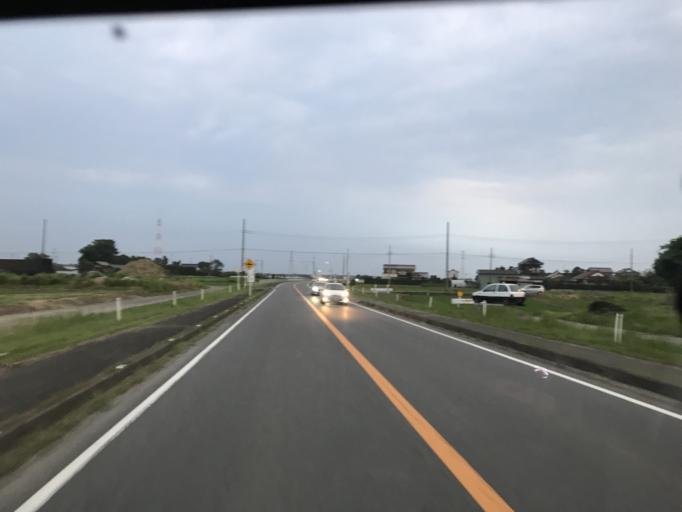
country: JP
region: Ibaraki
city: Ryugasaki
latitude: 35.8490
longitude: 140.1935
